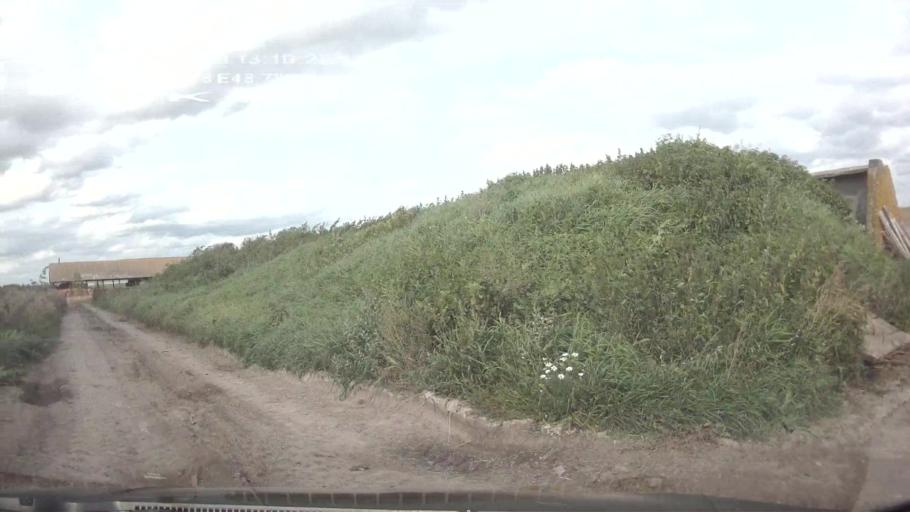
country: RU
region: Mariy-El
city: Kuzhener
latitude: 56.9691
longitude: 48.7867
